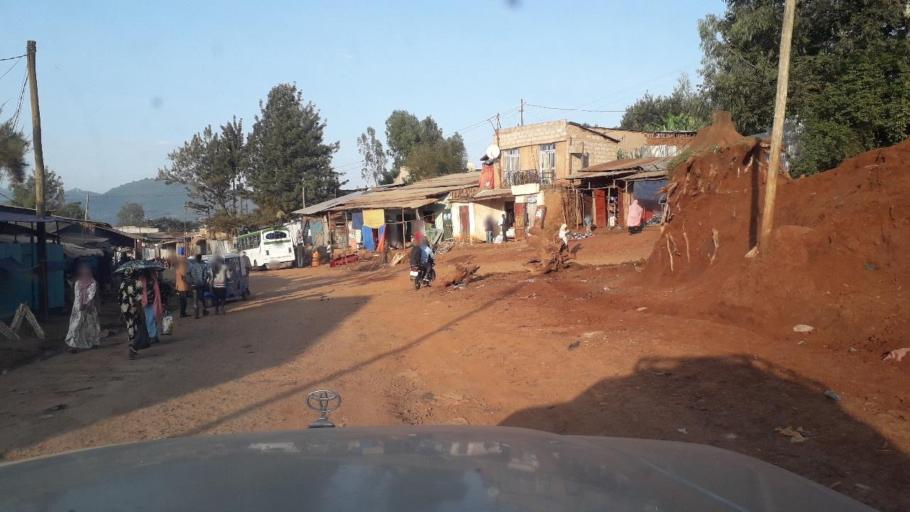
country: ET
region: Oromiya
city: Jima
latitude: 7.6403
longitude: 36.8414
